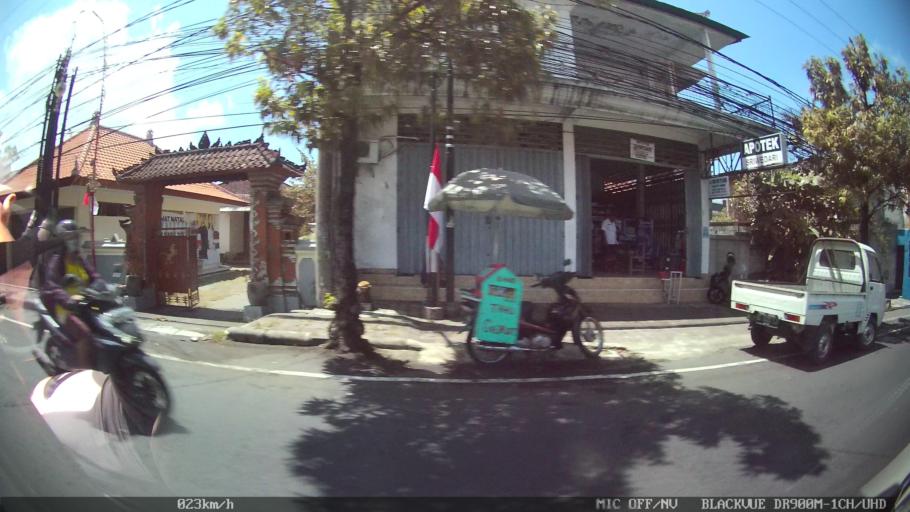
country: ID
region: Bali
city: Banjar Pasekan
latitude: -8.5988
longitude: 115.2830
